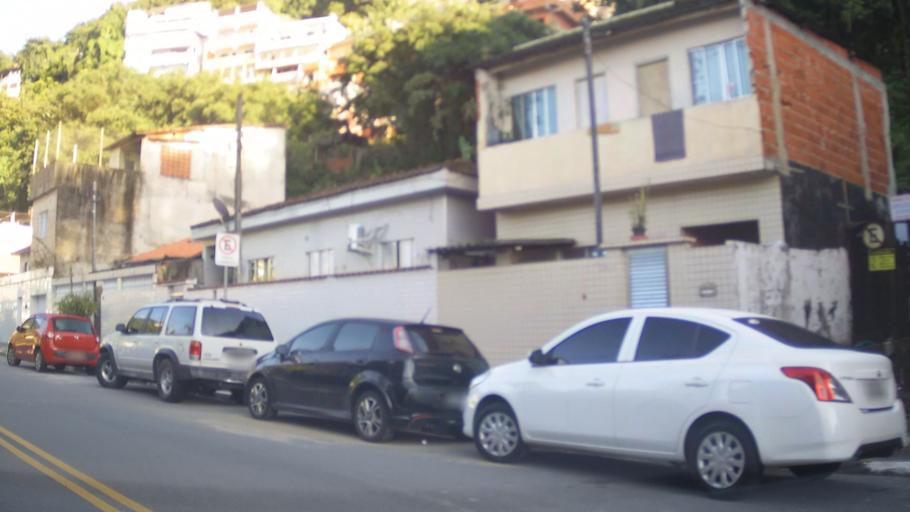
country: BR
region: Sao Paulo
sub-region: Santos
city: Santos
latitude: -23.9400
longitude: -46.3397
